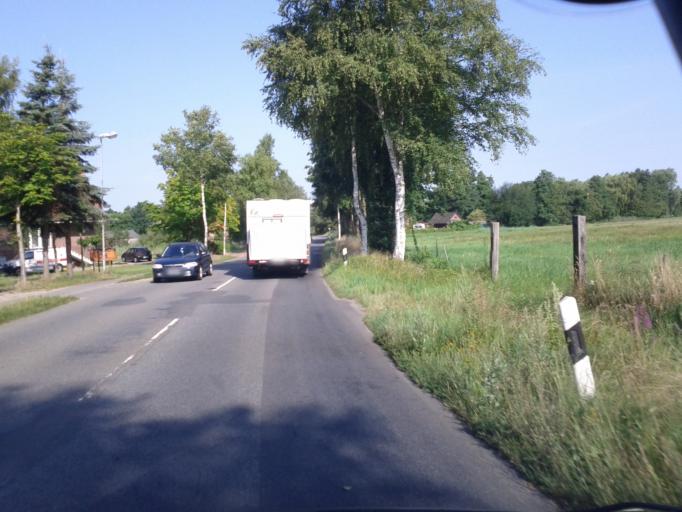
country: DE
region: Lower Saxony
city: Buxtehude
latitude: 53.4839
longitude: 9.6822
